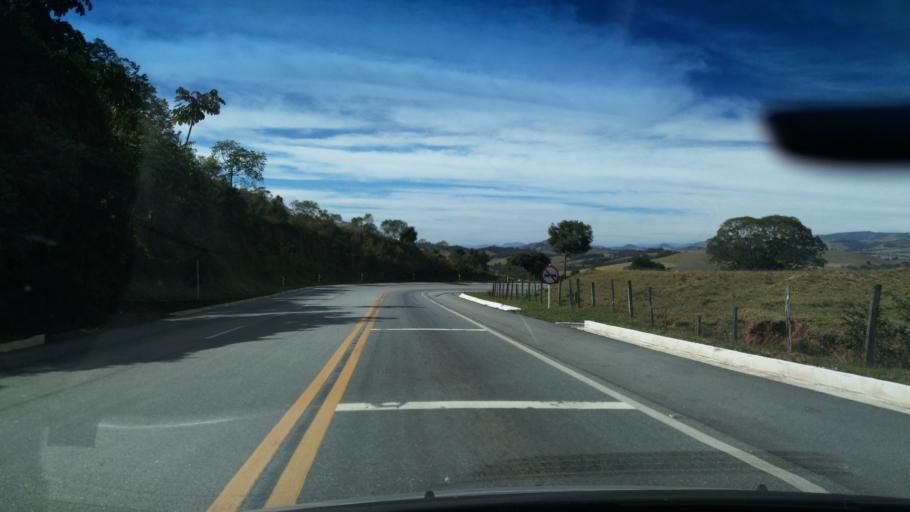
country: BR
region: Minas Gerais
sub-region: Borda Da Mata
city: Borda da Mata
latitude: -22.1296
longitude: -46.1476
